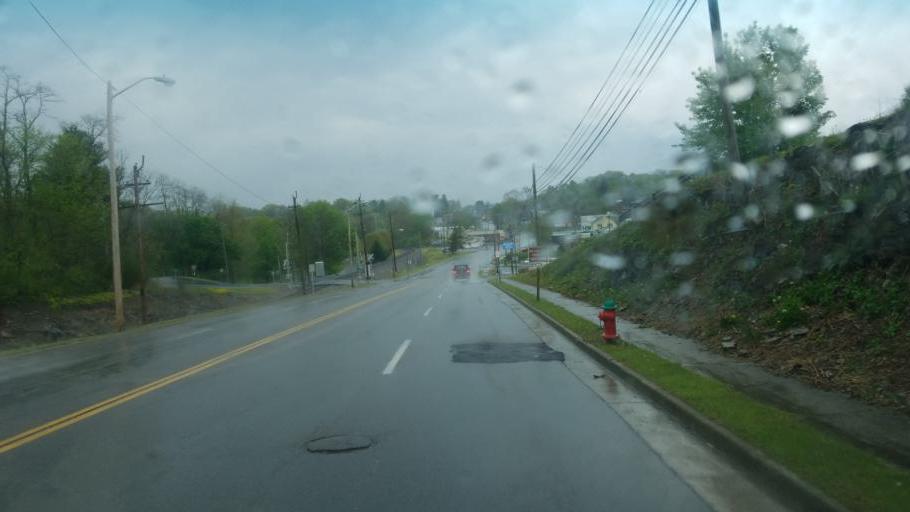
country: US
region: Virginia
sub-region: Smyth County
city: Marion
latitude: 36.8262
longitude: -81.5324
